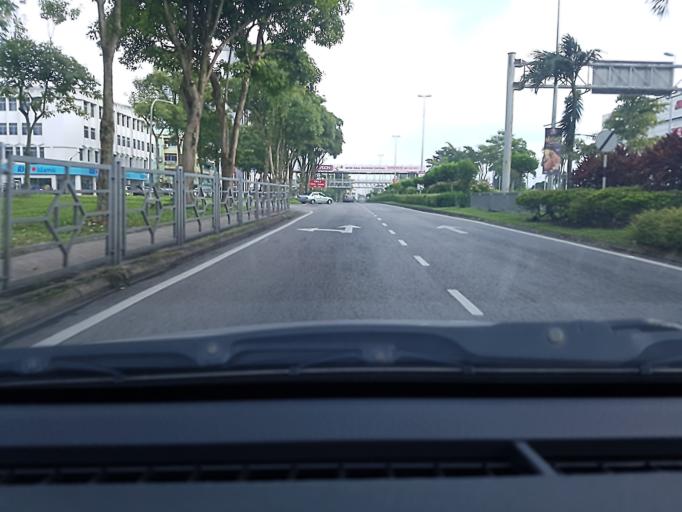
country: MY
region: Sarawak
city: Kuching
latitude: 1.5343
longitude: 110.3573
